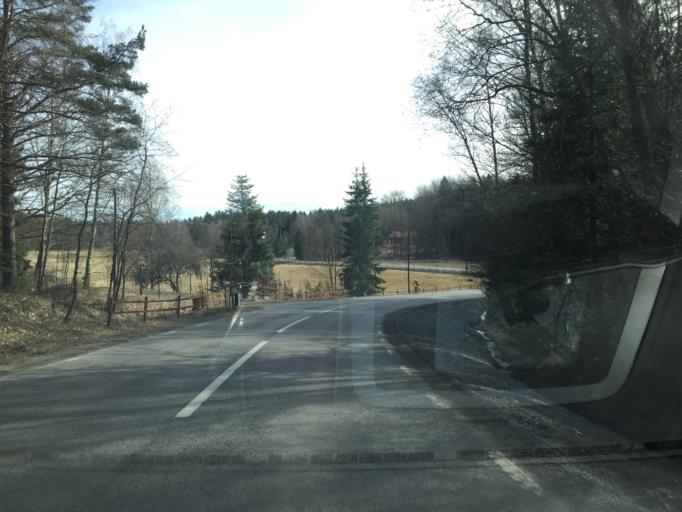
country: SE
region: Stockholm
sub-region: Haninge Kommun
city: Jordbro
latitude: 59.1203
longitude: 18.0132
